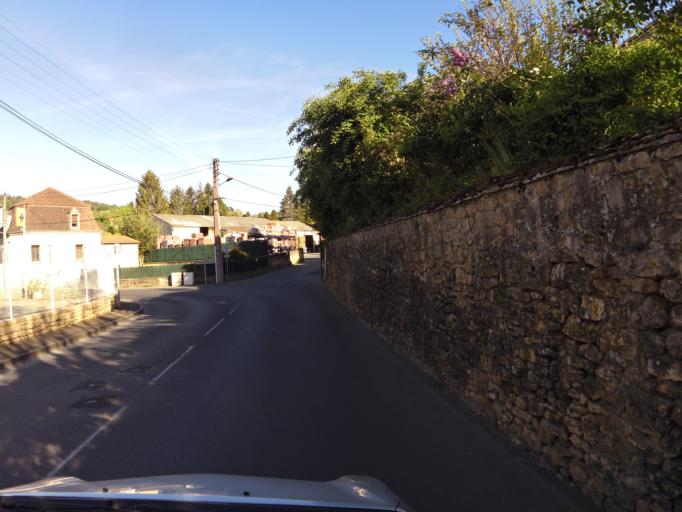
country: FR
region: Aquitaine
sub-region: Departement de la Dordogne
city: Sarlat-la-Caneda
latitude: 44.8977
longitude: 1.2146
